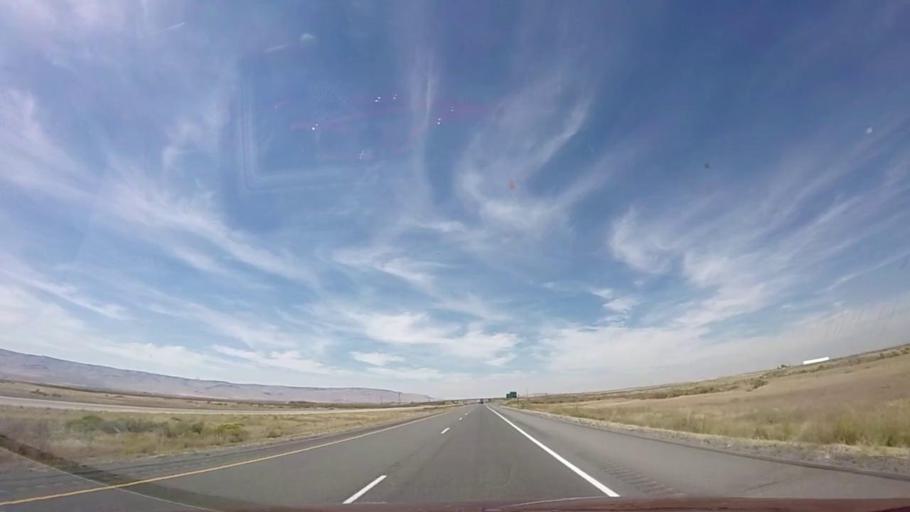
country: US
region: Idaho
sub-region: Minidoka County
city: Rupert
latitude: 42.4108
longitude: -113.3138
